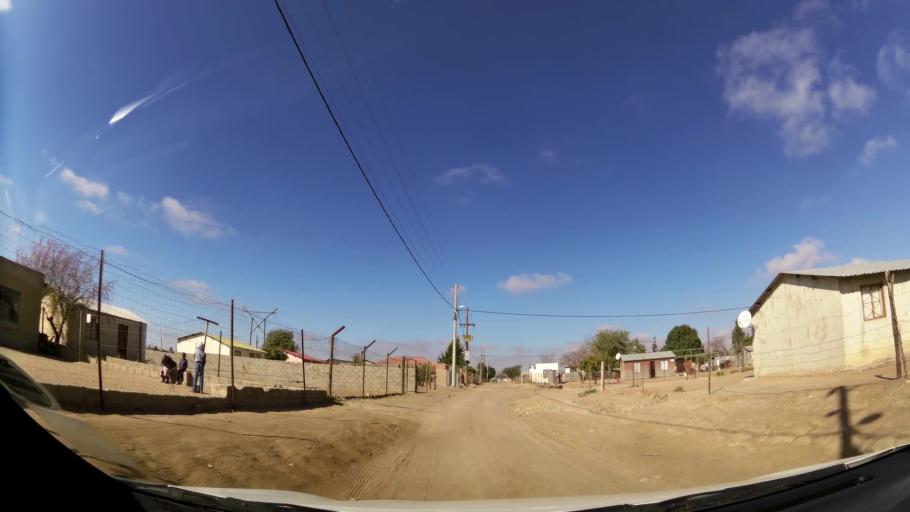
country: ZA
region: Limpopo
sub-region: Capricorn District Municipality
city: Polokwane
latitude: -23.8472
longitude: 29.4054
